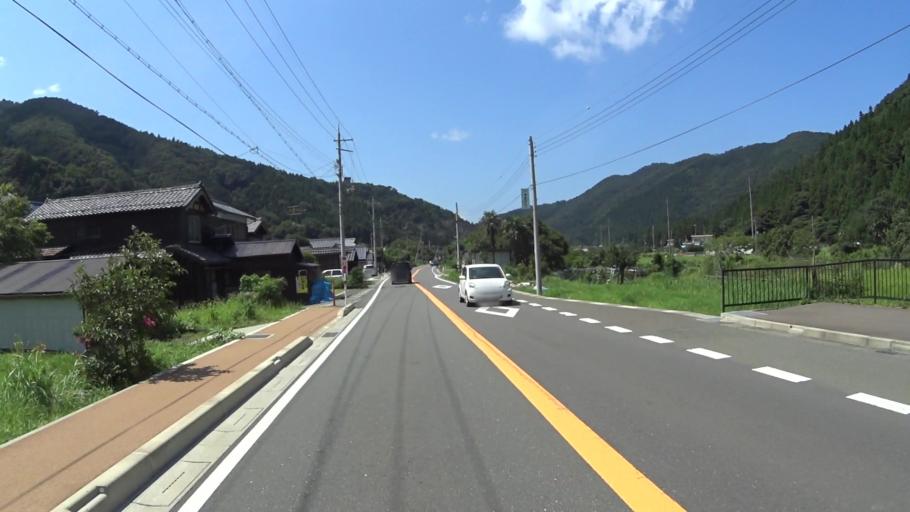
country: JP
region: Fukui
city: Obama
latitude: 35.4425
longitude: 135.9038
